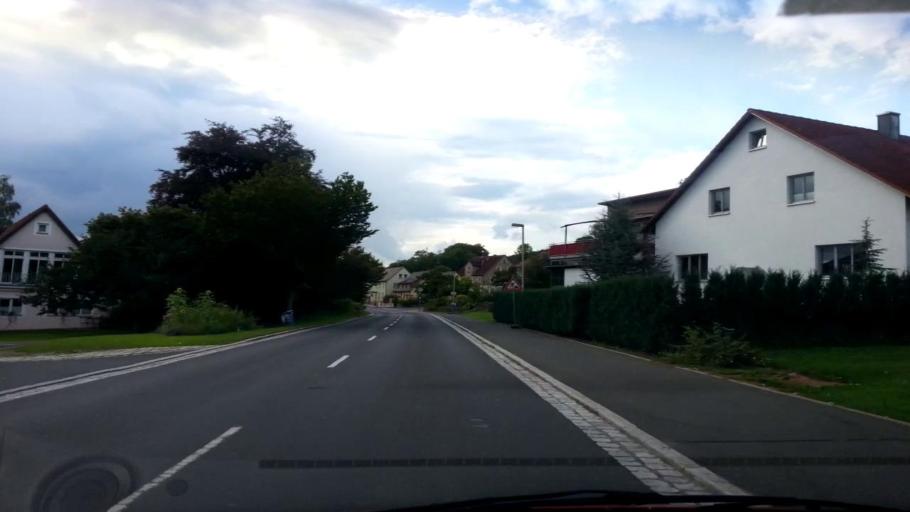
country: DE
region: Bavaria
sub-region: Regierungsbezirk Mittelfranken
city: Burghaslach
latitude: 49.7338
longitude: 10.6008
